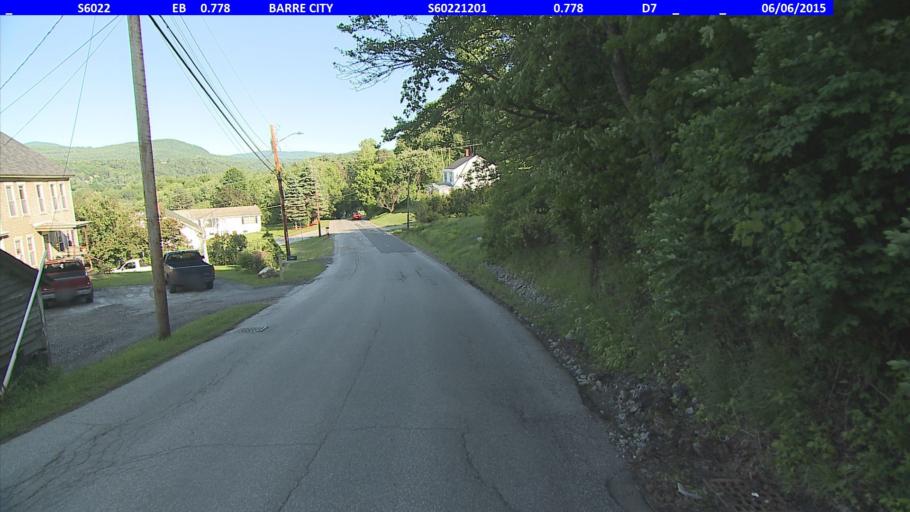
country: US
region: Vermont
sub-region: Washington County
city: Barre
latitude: 44.1964
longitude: -72.5119
